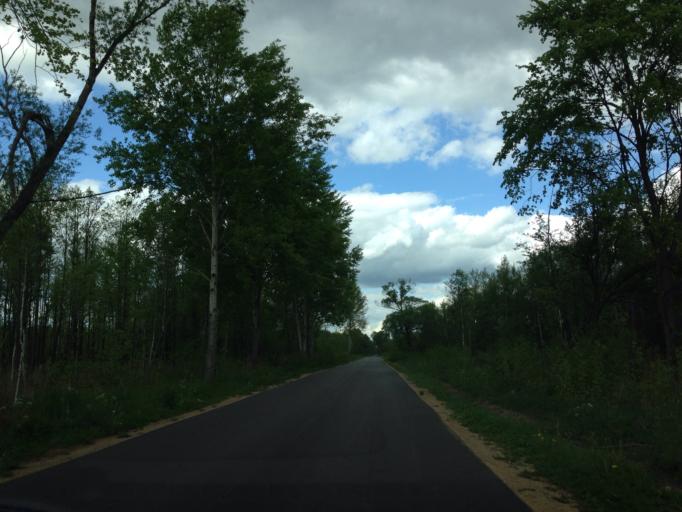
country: PL
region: Podlasie
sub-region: Powiat bialostocki
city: Tykocin
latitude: 53.3073
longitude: 22.6037
